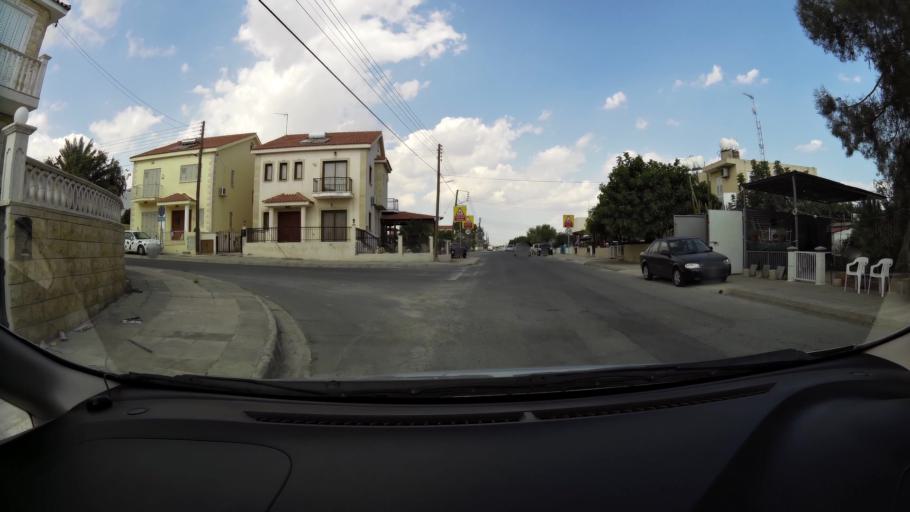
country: CY
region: Larnaka
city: Dhromolaxia
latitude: 34.9062
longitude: 33.5925
